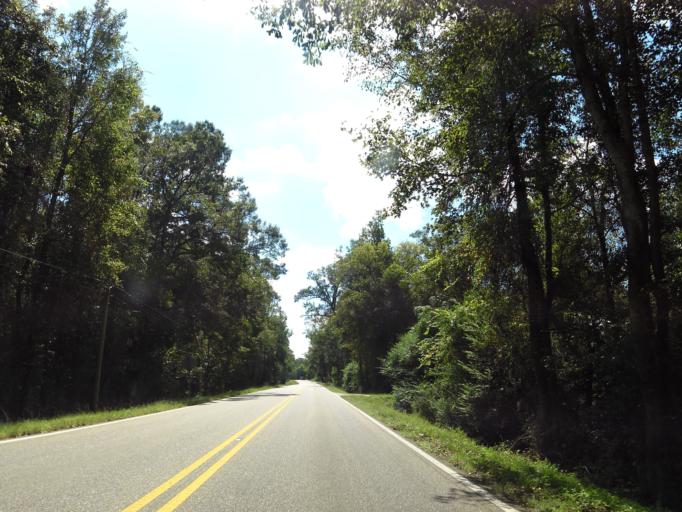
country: US
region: Alabama
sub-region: Dallas County
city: Selma
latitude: 32.3890
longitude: -87.0854
